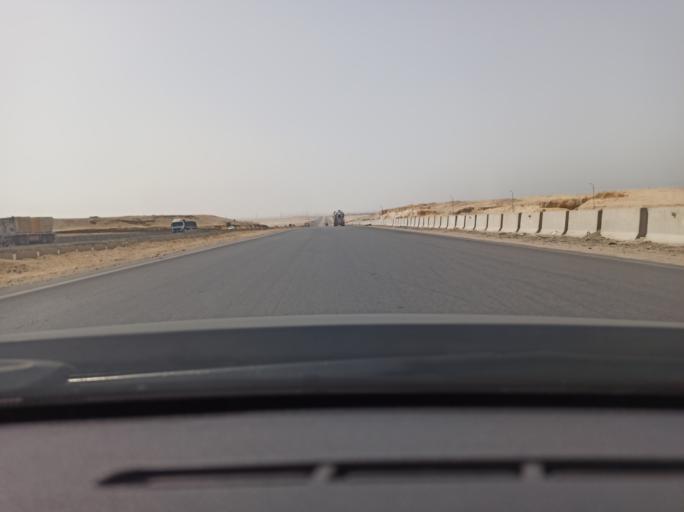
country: EG
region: Muhafazat al Fayyum
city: Al Wasitah
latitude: 29.3746
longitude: 31.3100
